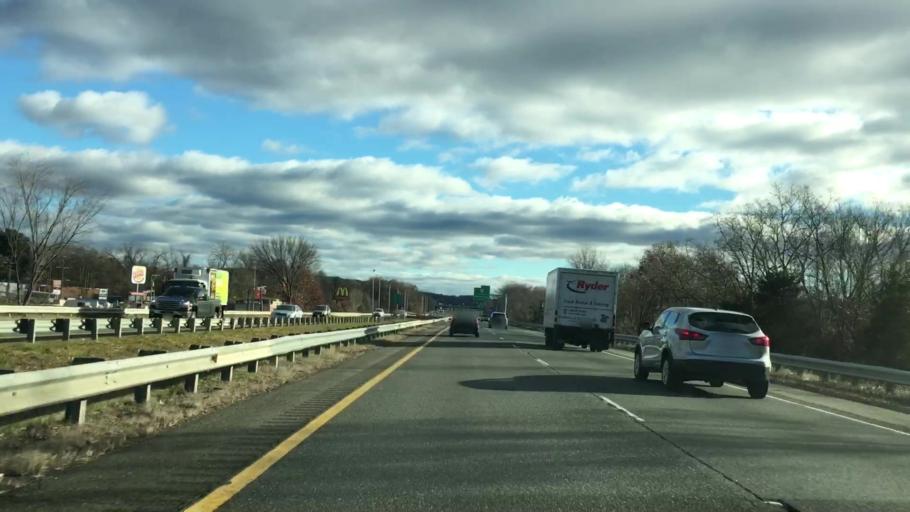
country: US
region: Massachusetts
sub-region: Hampden County
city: Ludlow
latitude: 42.1669
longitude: -72.4839
